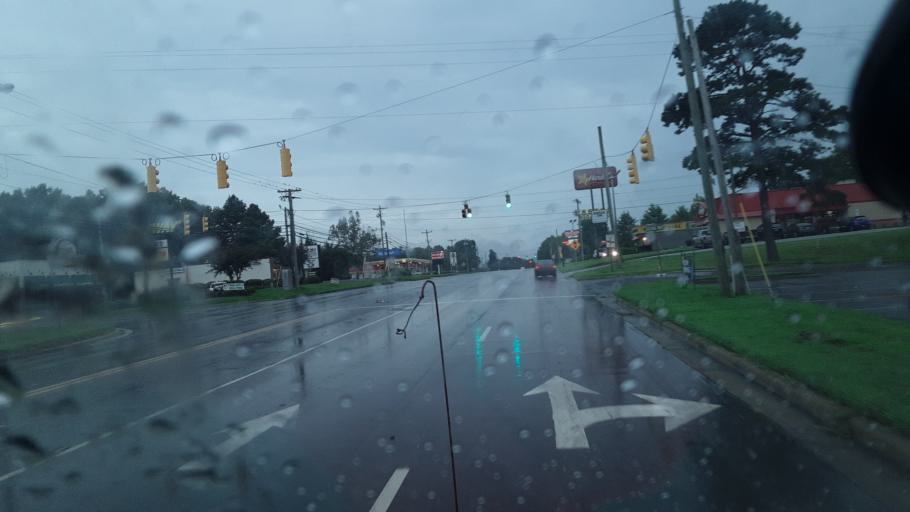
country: US
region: North Carolina
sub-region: Surry County
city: Toast
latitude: 36.4758
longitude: -80.6193
